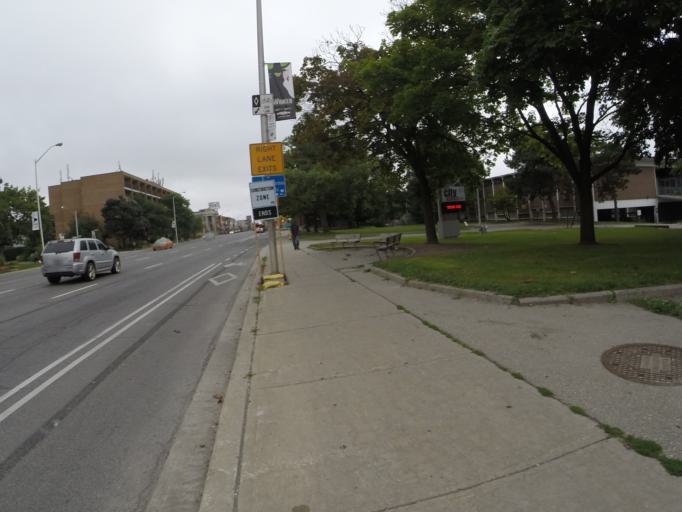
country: CA
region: Ontario
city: Toronto
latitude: 43.6754
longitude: -79.3626
